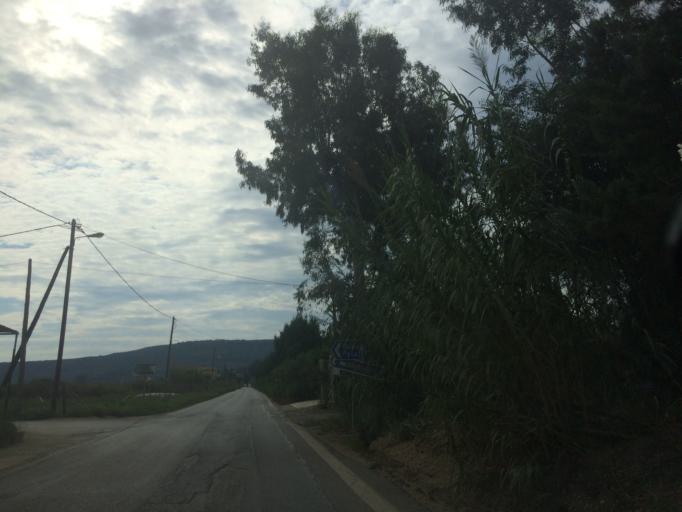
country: GR
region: Peloponnese
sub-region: Nomos Messinias
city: Pylos
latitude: 36.9463
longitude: 21.7083
